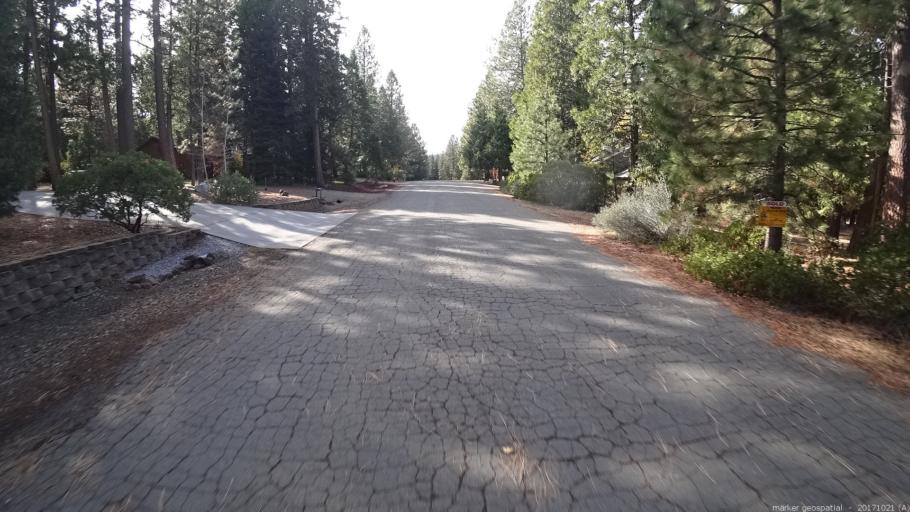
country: US
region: California
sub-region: Shasta County
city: Burney
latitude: 40.8730
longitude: -121.6643
